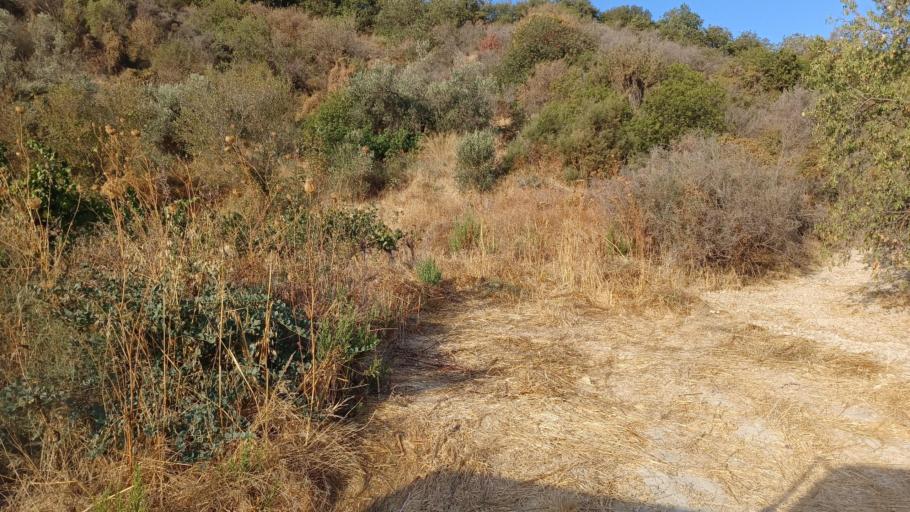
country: CY
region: Pafos
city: Polis
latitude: 34.9500
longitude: 32.4744
